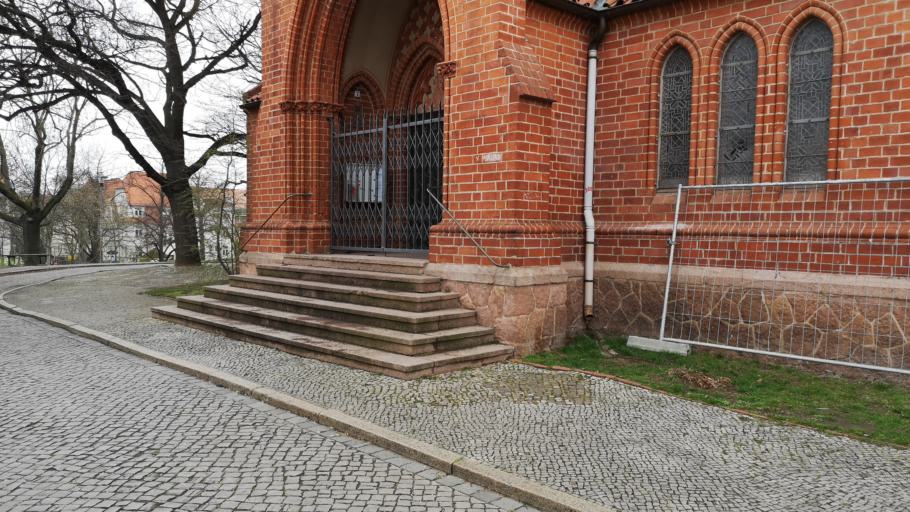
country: DE
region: Saxony-Anhalt
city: Halle (Saale)
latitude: 51.4956
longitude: 11.9739
